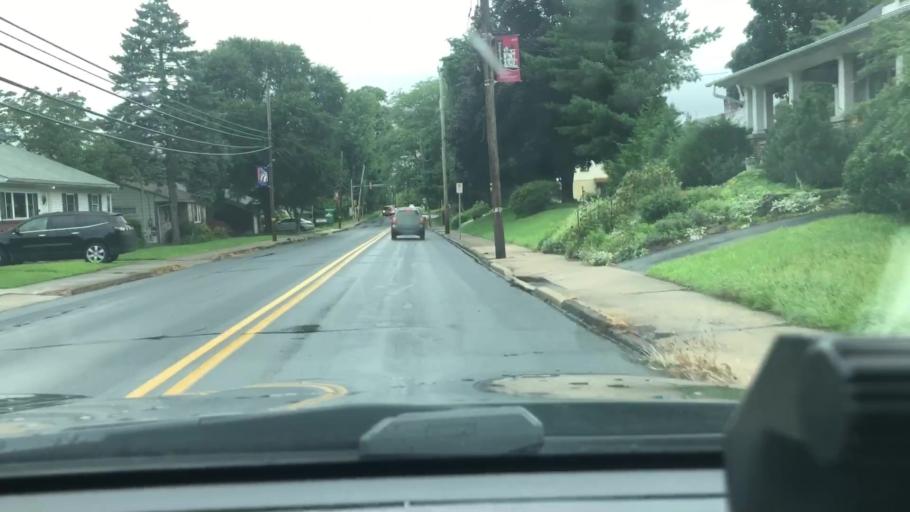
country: US
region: Pennsylvania
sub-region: Lehigh County
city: Coopersburg
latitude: 40.5150
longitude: -75.3901
